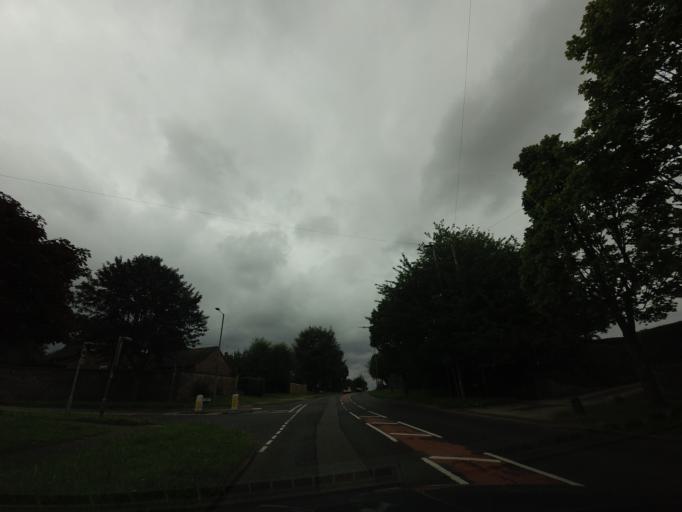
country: GB
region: England
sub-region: Nottinghamshire
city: Kimberley
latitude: 53.0082
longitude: -1.2545
